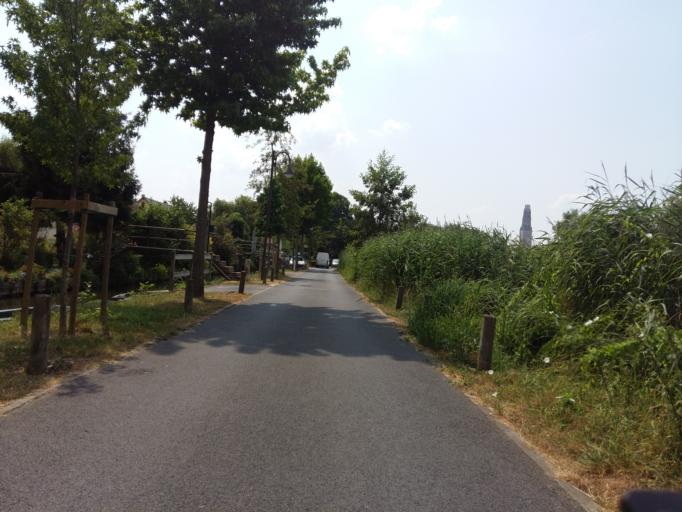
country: FR
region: Picardie
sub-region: Departement de la Somme
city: Rivery
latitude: 49.8970
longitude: 2.3159
